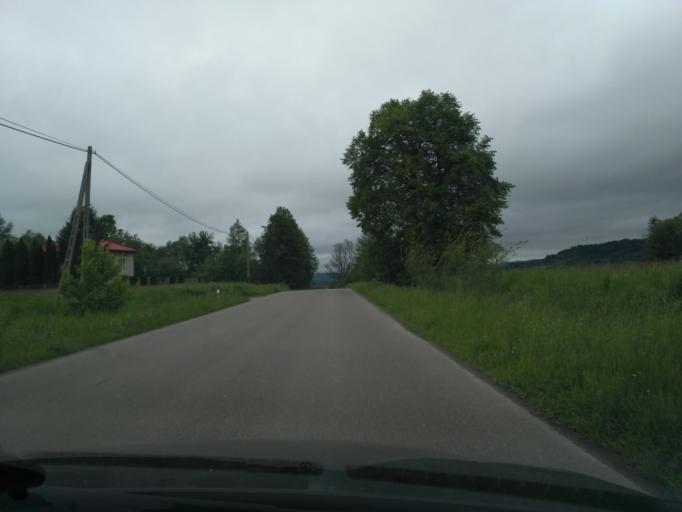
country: PL
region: Subcarpathian Voivodeship
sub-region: Powiat jasielski
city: Brzyska
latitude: 49.8293
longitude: 21.3941
